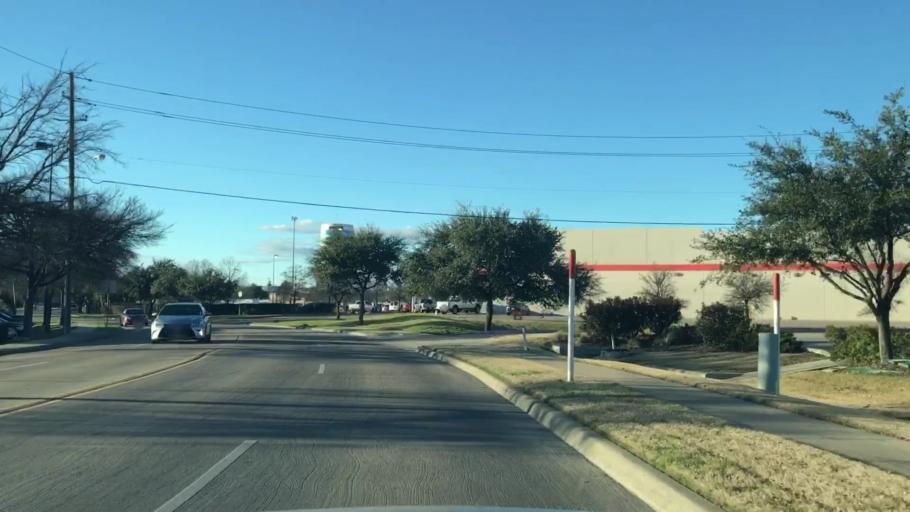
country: US
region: Texas
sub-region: Rockwall County
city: Rockwall
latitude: 32.8965
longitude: -96.4605
